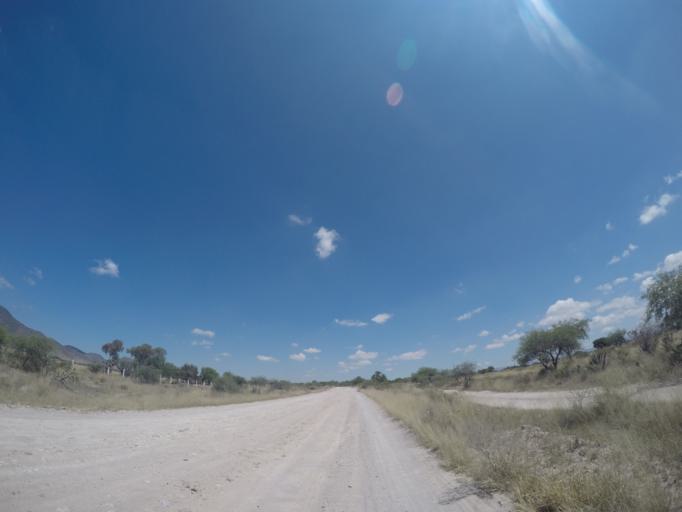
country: MX
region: San Luis Potosi
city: La Pila
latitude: 21.9928
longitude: -100.8990
